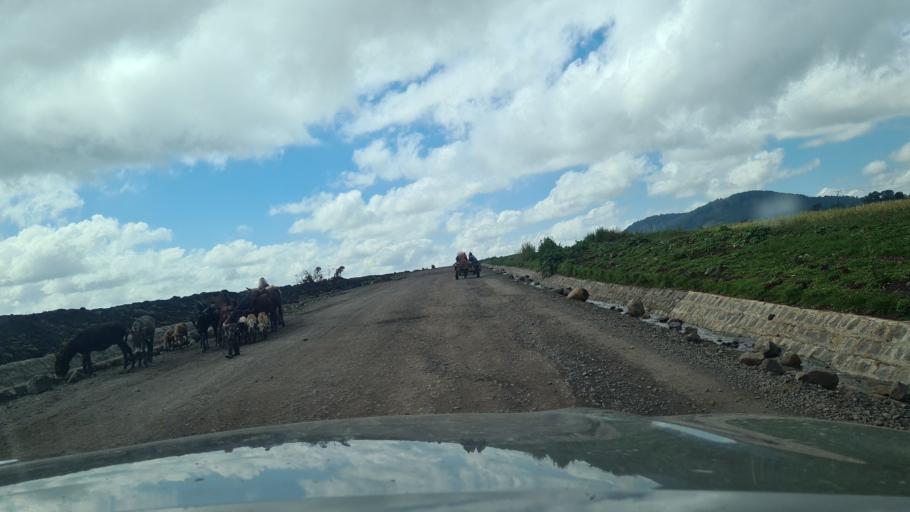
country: ET
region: Oromiya
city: Huruta
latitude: 8.0951
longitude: 39.5351
